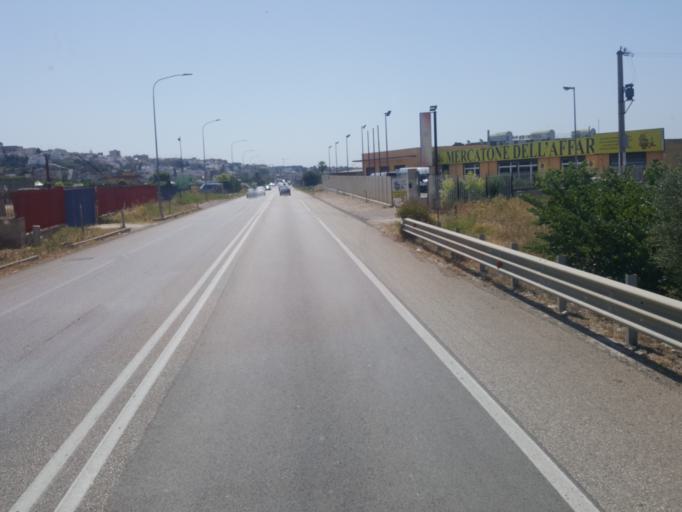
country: IT
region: Apulia
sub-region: Provincia di Taranto
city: Massafra
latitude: 40.5907
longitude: 17.0977
